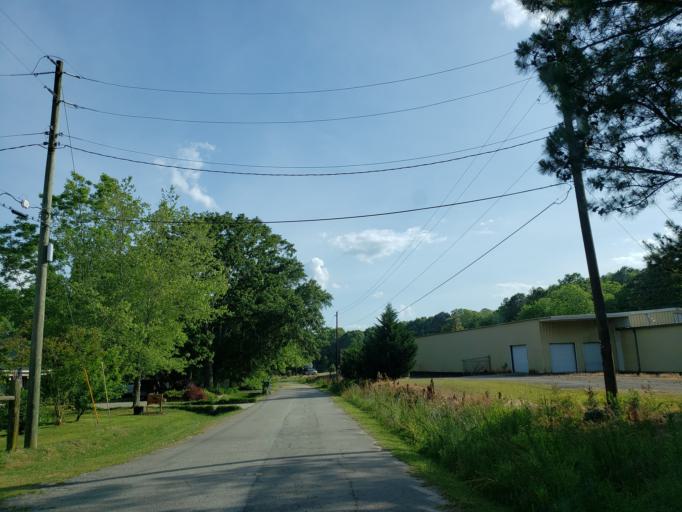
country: US
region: Georgia
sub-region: Carroll County
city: Carrollton
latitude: 33.4502
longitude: -85.1326
